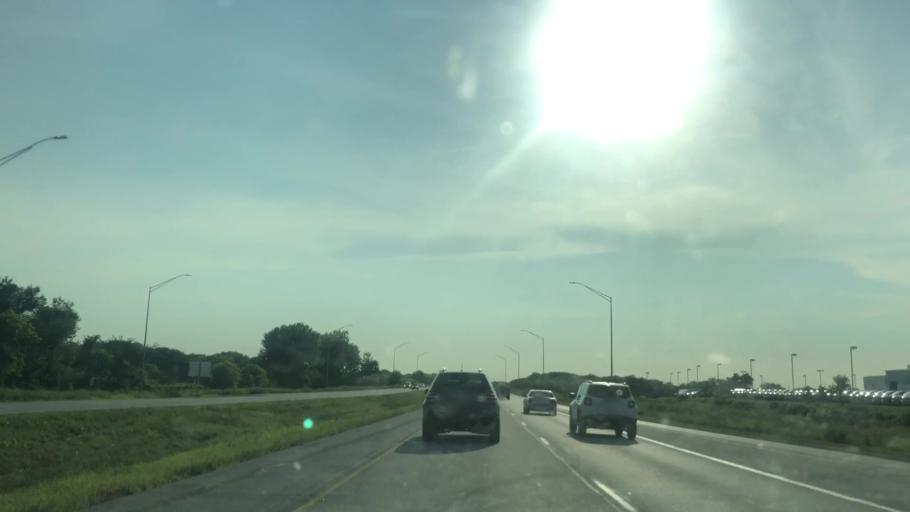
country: US
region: Iowa
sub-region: Story County
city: Ames
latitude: 42.0065
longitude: -93.5892
